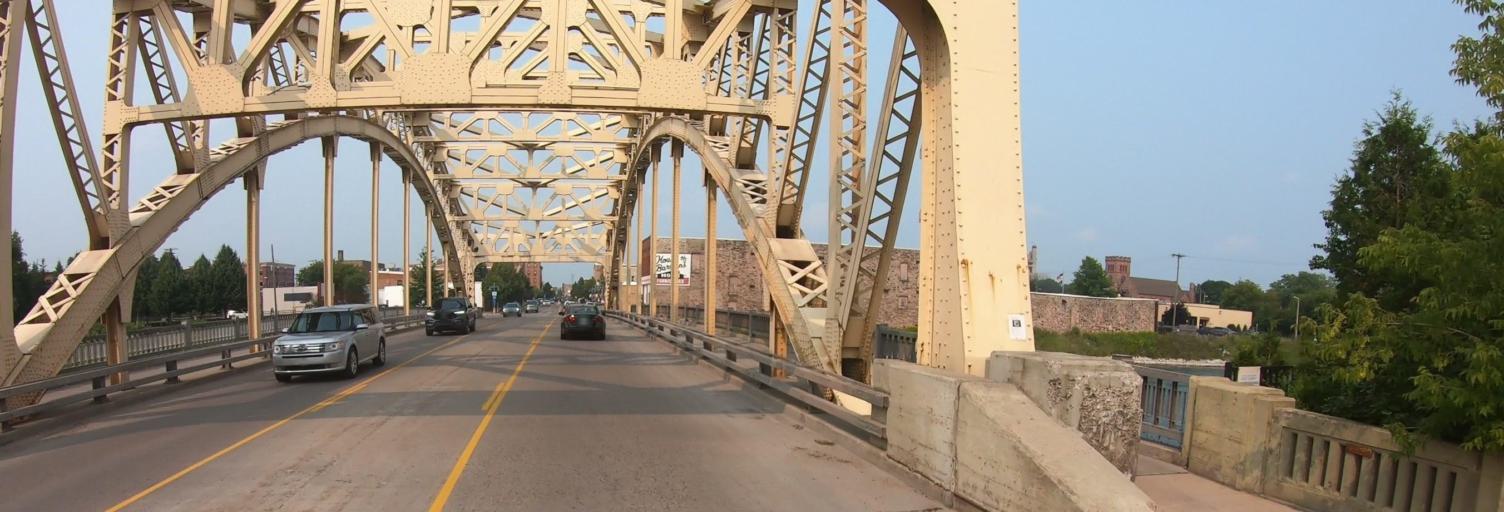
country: US
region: Michigan
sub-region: Chippewa County
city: Sault Ste. Marie
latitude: 46.4949
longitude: -84.3497
